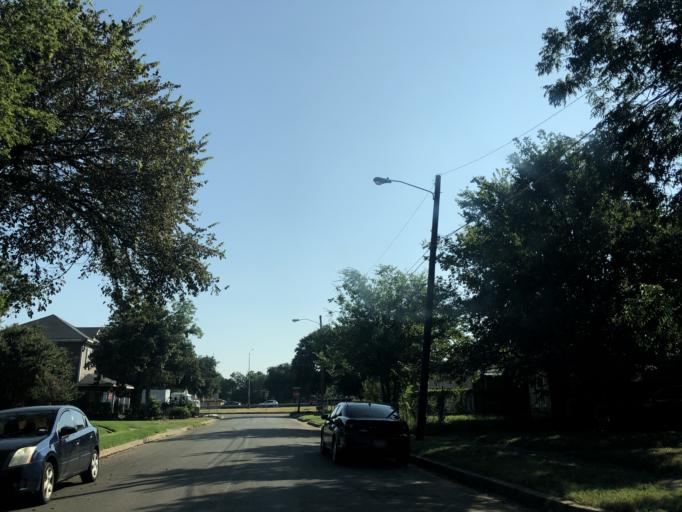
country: US
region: Texas
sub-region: Dallas County
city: Dallas
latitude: 32.7536
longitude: -96.7665
